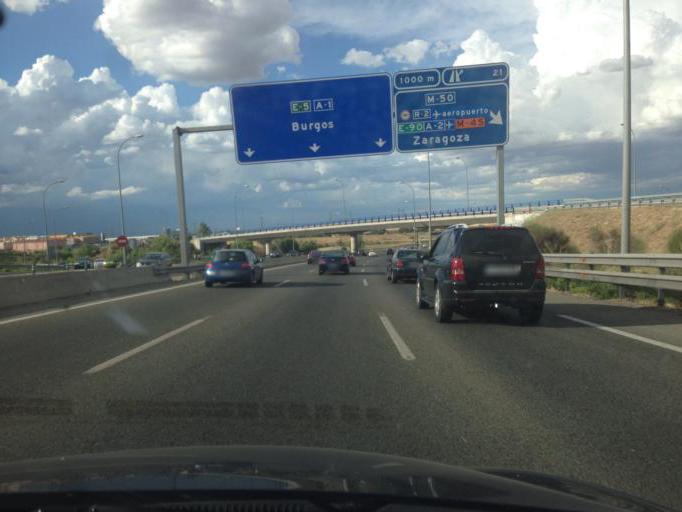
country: ES
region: Madrid
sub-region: Provincia de Madrid
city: San Sebastian de los Reyes
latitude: 40.5517
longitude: -3.6075
